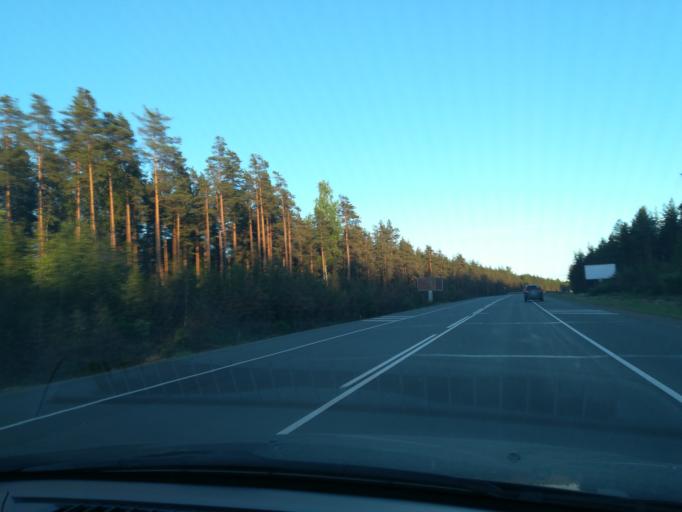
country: RU
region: Leningrad
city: Yakovlevo
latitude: 60.4237
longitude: 29.3799
